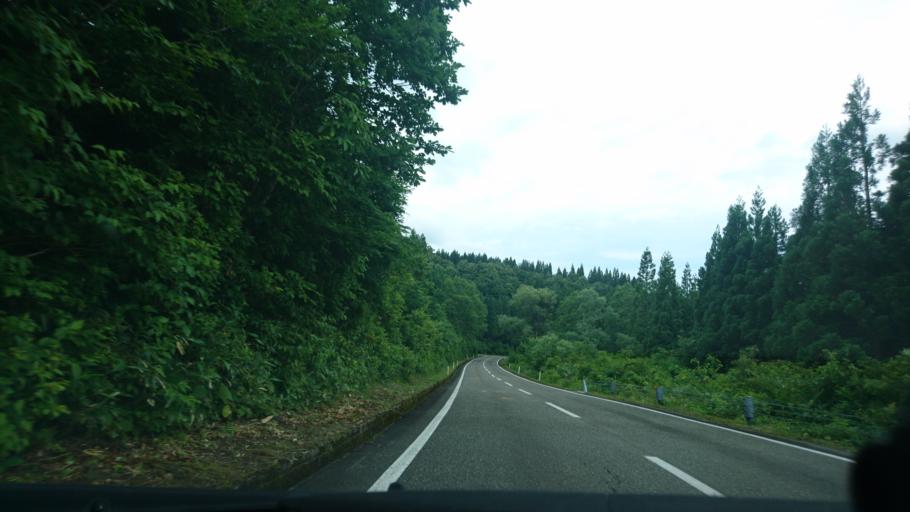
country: JP
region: Akita
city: Yuzawa
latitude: 39.1603
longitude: 140.7479
